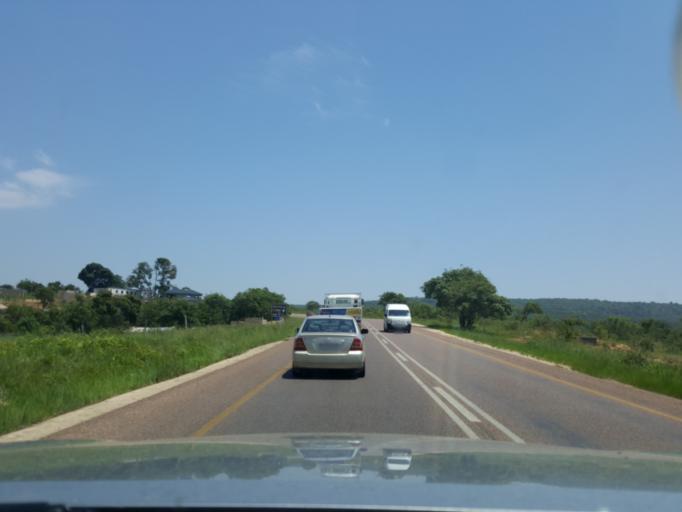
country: ZA
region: Limpopo
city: Thulamahashi
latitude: -24.8964
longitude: 31.1066
